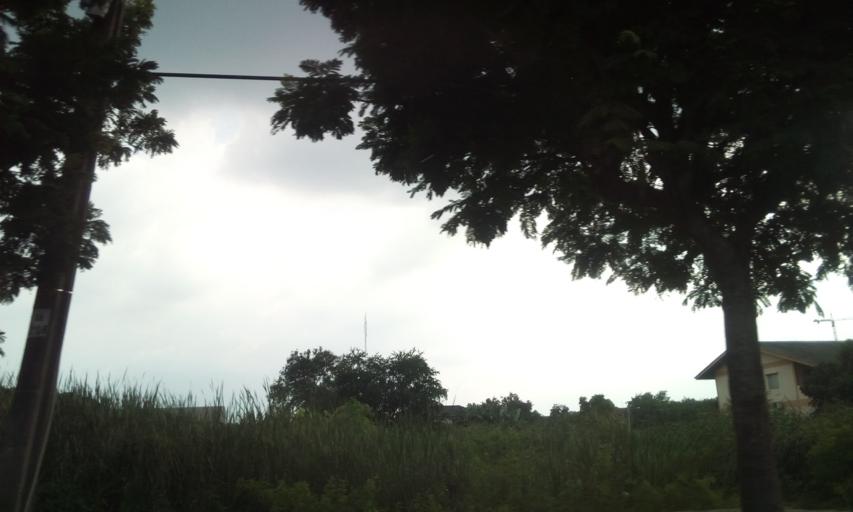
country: TH
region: Bangkok
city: Don Mueang
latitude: 13.9377
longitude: 100.5557
